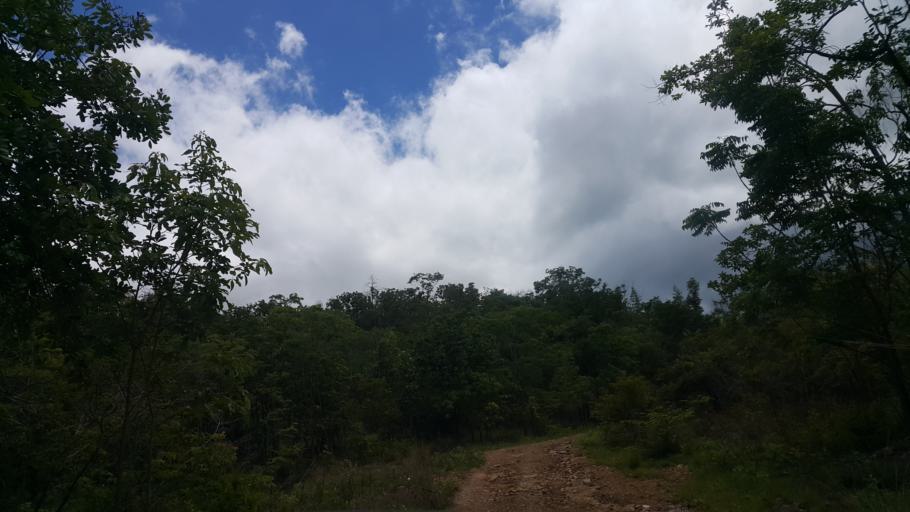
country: TH
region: Sukhothai
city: Thung Saliam
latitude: 17.3309
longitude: 99.4710
